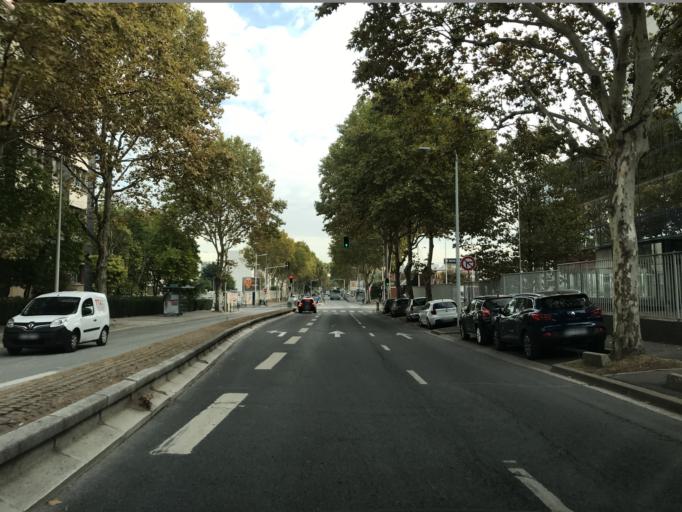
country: FR
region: Ile-de-France
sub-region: Departement des Hauts-de-Seine
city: La Defense
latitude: 48.9006
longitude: 2.2243
